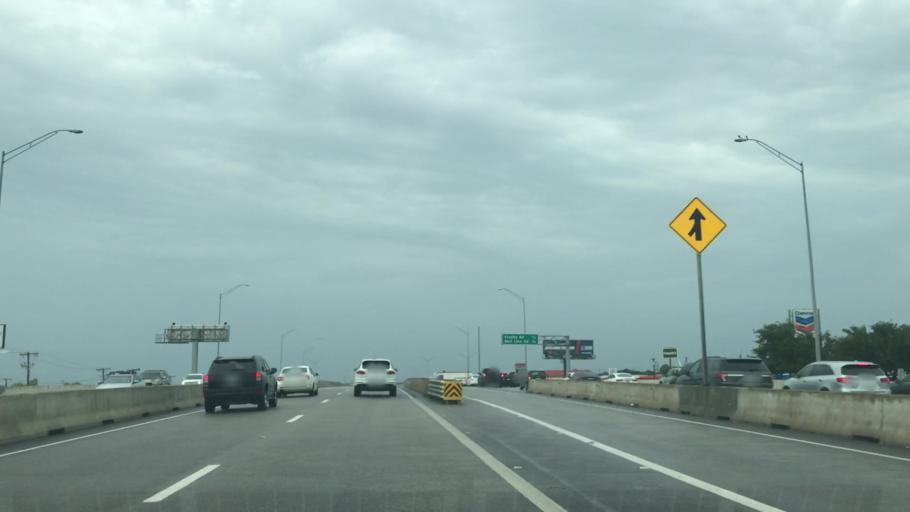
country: US
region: Texas
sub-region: Dallas County
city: Carrollton
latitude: 32.9544
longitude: -96.9035
